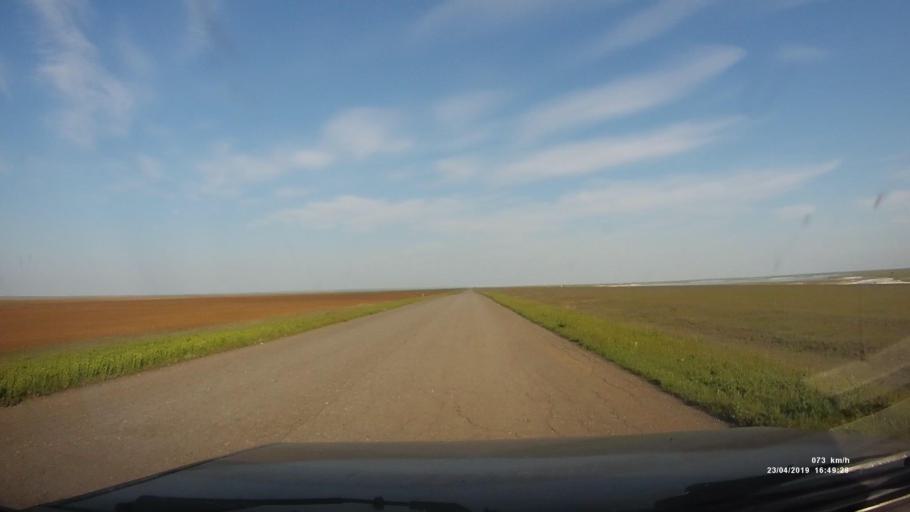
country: RU
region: Kalmykiya
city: Priyutnoye
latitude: 46.3309
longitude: 43.2770
